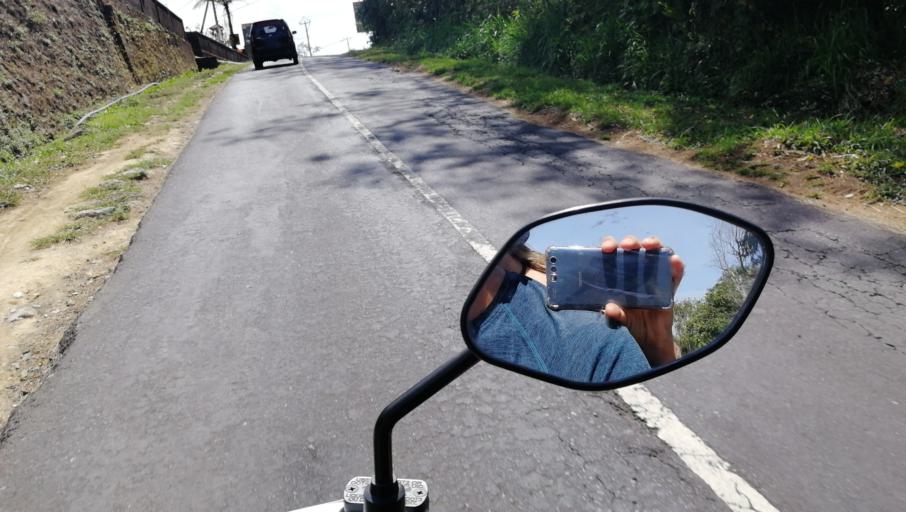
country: ID
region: Bali
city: Munduk
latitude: -8.2377
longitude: 115.1156
